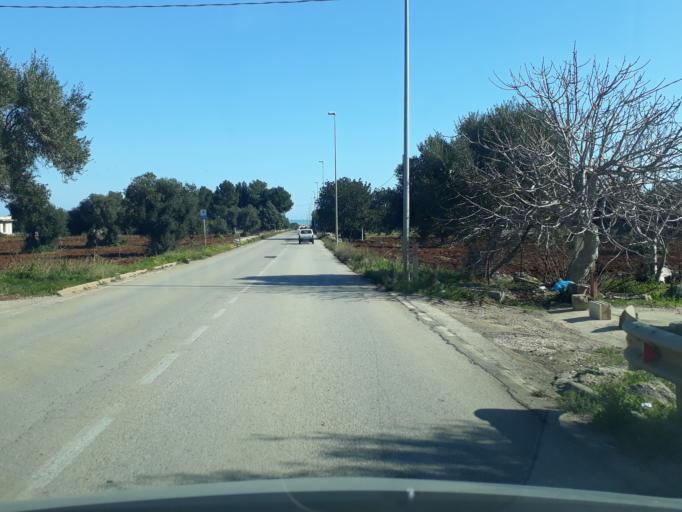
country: IT
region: Apulia
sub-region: Provincia di Brindisi
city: Fasano
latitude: 40.8997
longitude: 17.3399
